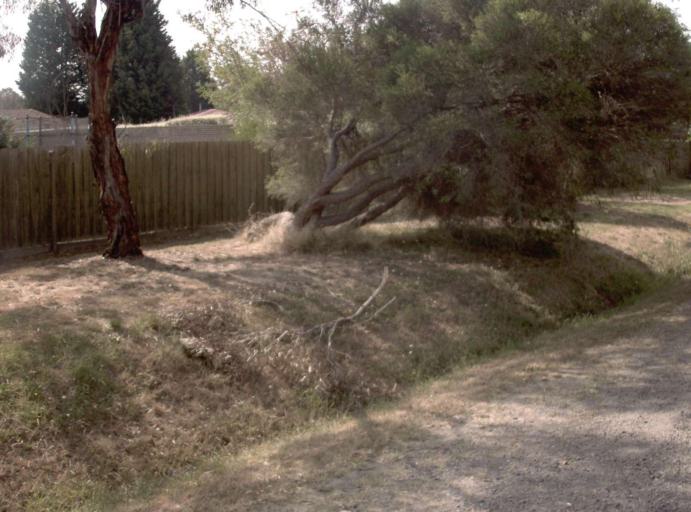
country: AU
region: Victoria
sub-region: Yarra Ranges
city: Lysterfield
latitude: -37.9166
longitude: 145.2712
